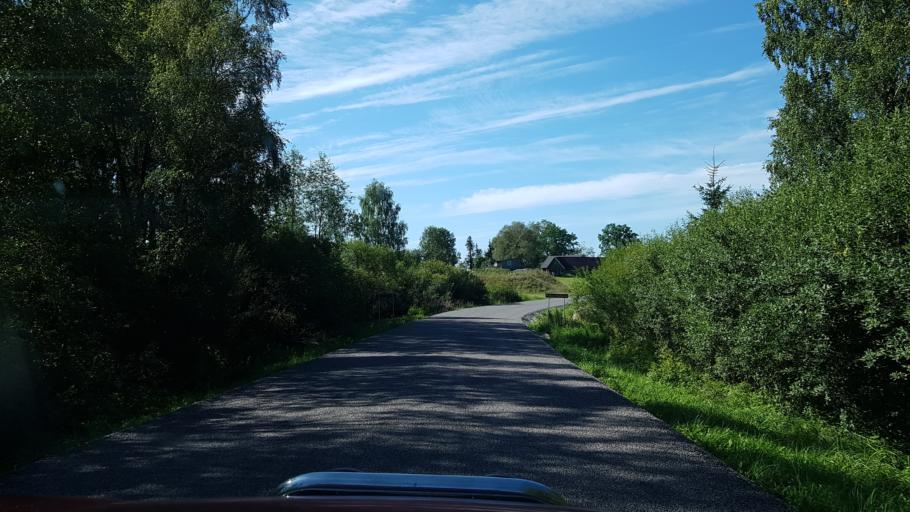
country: EE
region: Tartu
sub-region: Elva linn
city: Elva
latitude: 58.2491
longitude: 26.3707
